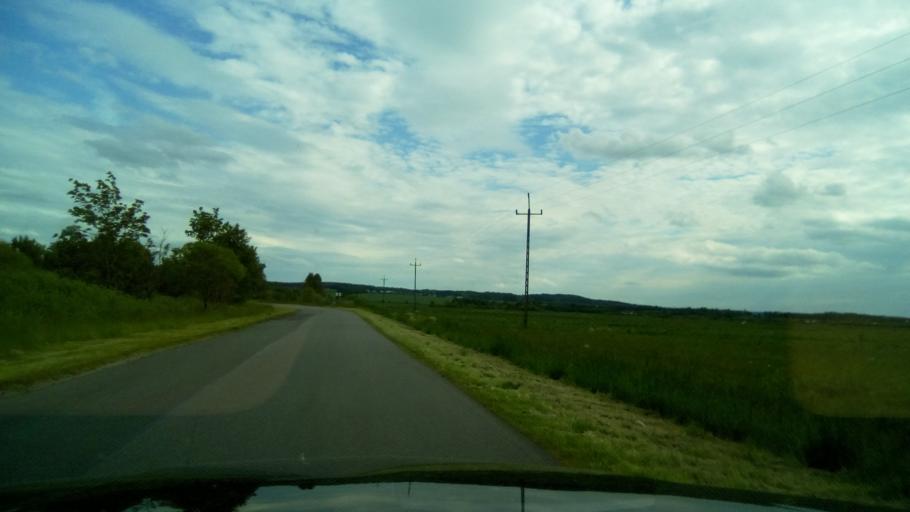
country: PL
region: Pomeranian Voivodeship
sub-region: Powiat pucki
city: Krokowa
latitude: 54.8148
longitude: 18.0877
